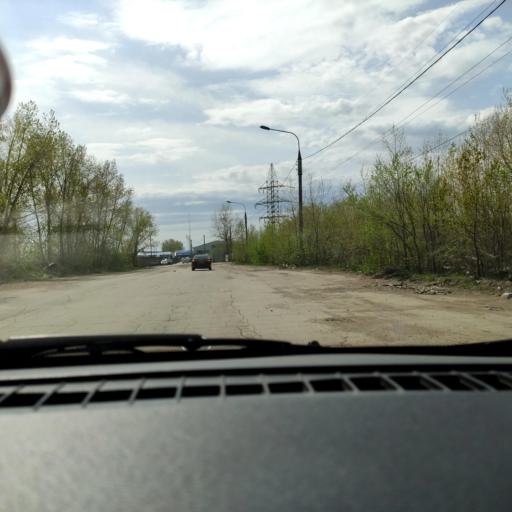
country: RU
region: Samara
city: Samara
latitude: 53.1773
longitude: 50.1240
